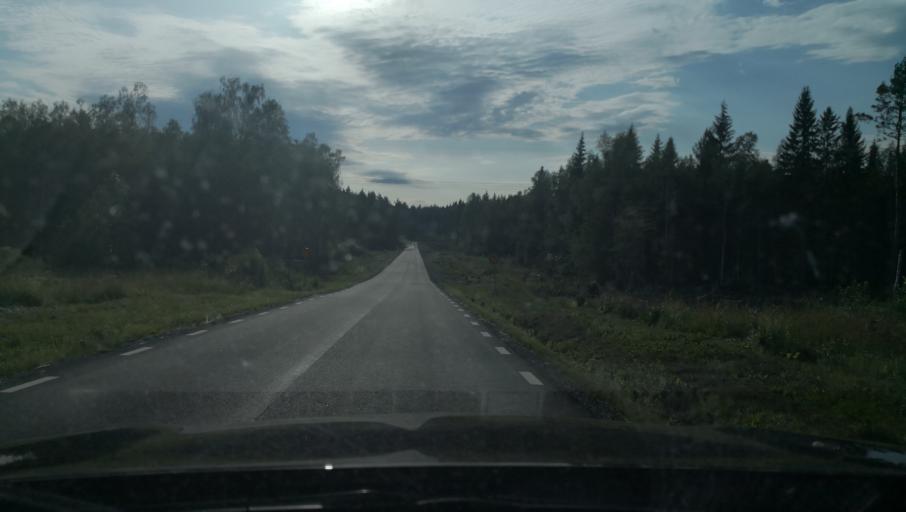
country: SE
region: Dalarna
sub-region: Smedjebackens Kommun
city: Smedjebacken
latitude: 60.0394
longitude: 15.3193
